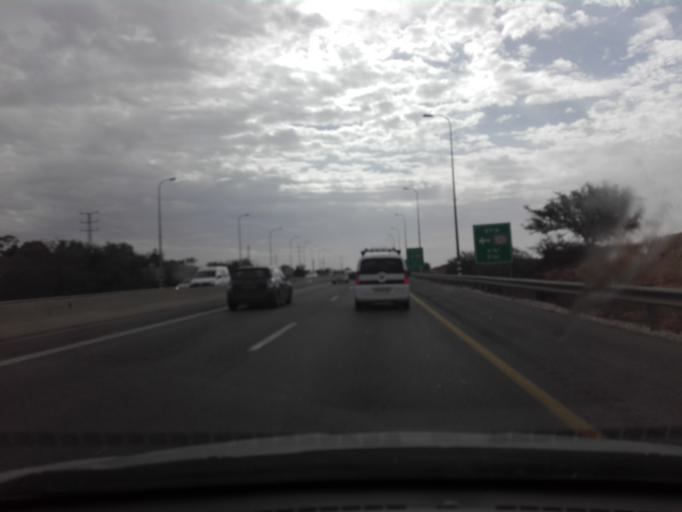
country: IL
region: Southern District
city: Lehavim
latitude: 31.3180
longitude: 34.7873
